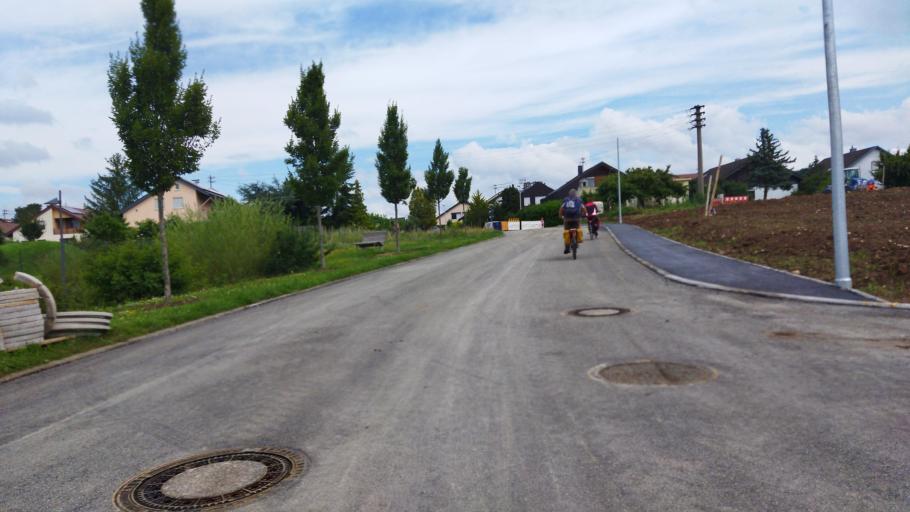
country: DE
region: Baden-Wuerttemberg
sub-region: Regierungsbezirk Stuttgart
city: Hessigheim
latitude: 48.9952
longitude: 9.1815
